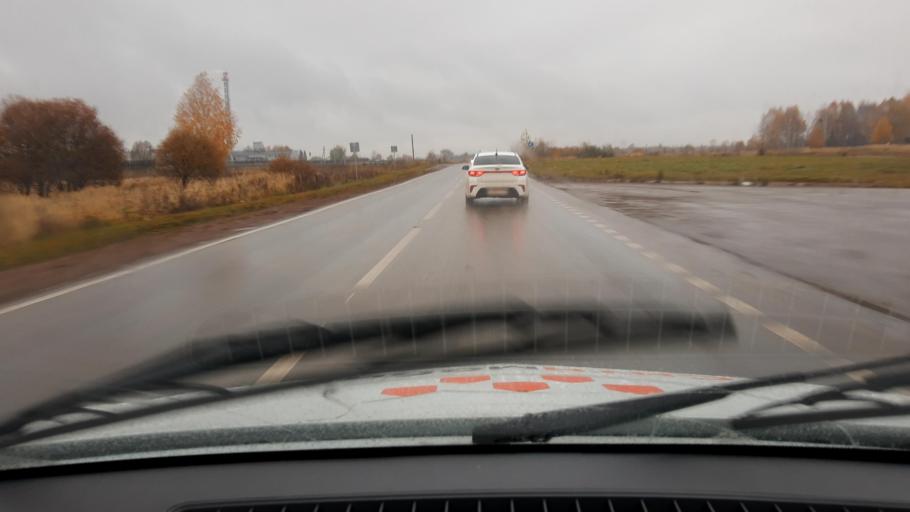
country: RU
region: Bashkortostan
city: Kabakovo
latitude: 54.7371
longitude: 56.2034
